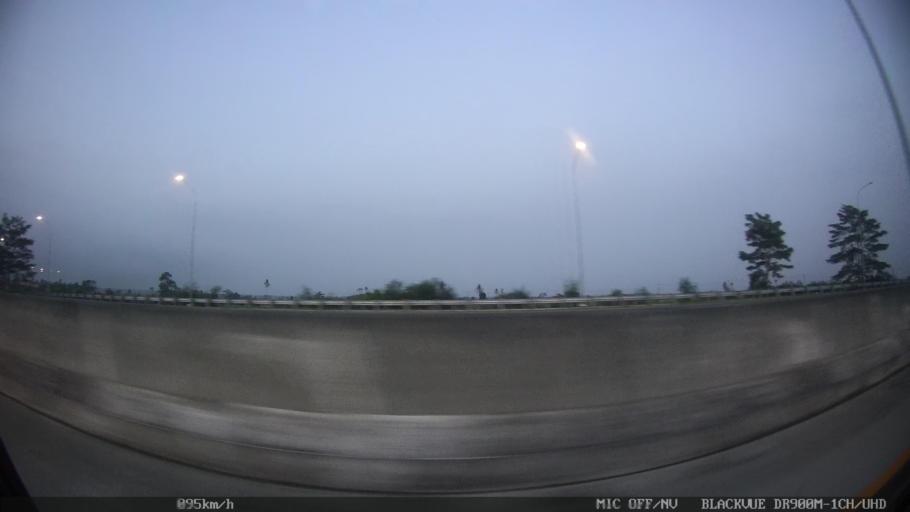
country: ID
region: Lampung
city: Sidorejo
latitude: -5.6125
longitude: 105.5588
